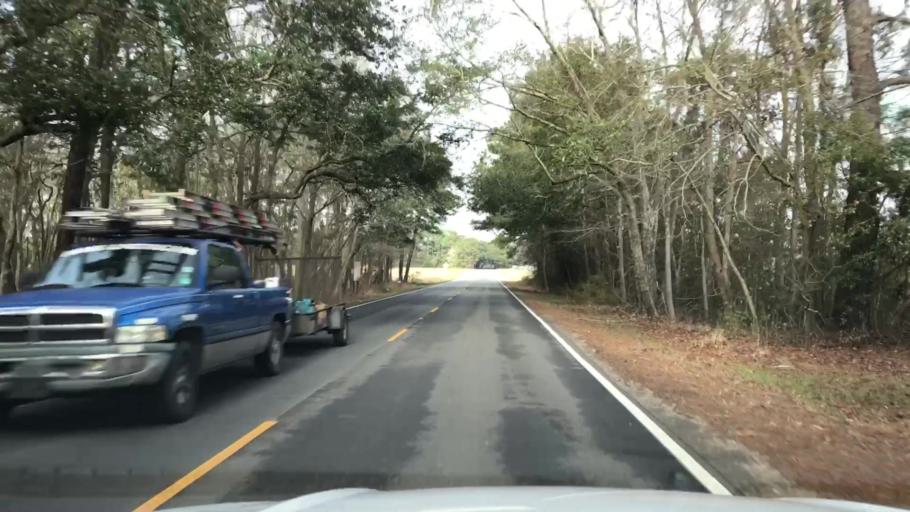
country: US
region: South Carolina
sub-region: Charleston County
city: Folly Beach
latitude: 32.7023
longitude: -80.0152
